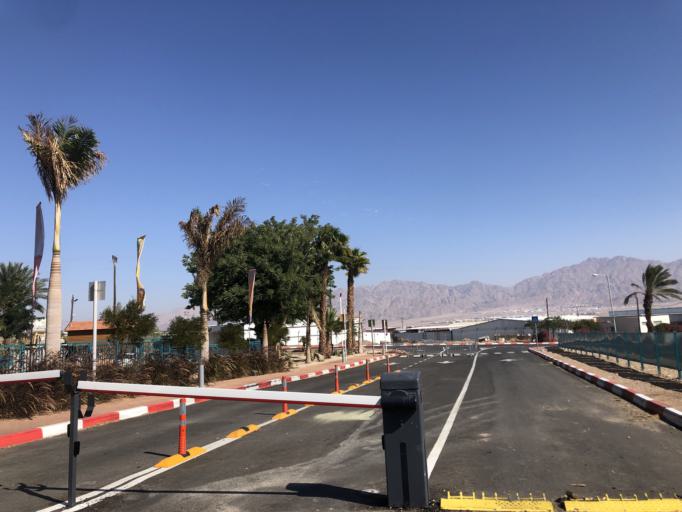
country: IL
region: Southern District
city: Eilat
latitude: 29.5798
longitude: 34.9637
